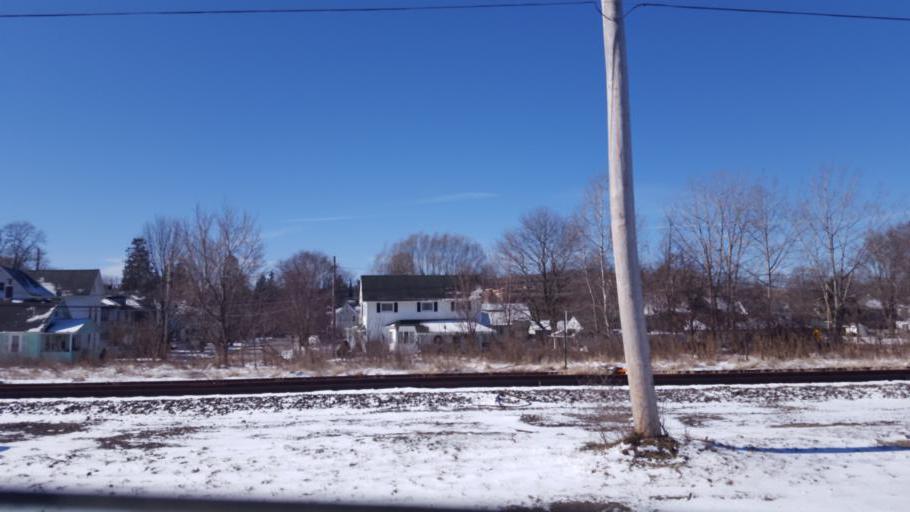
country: US
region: New York
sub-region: Allegany County
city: Wellsville
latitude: 42.1263
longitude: -77.9510
